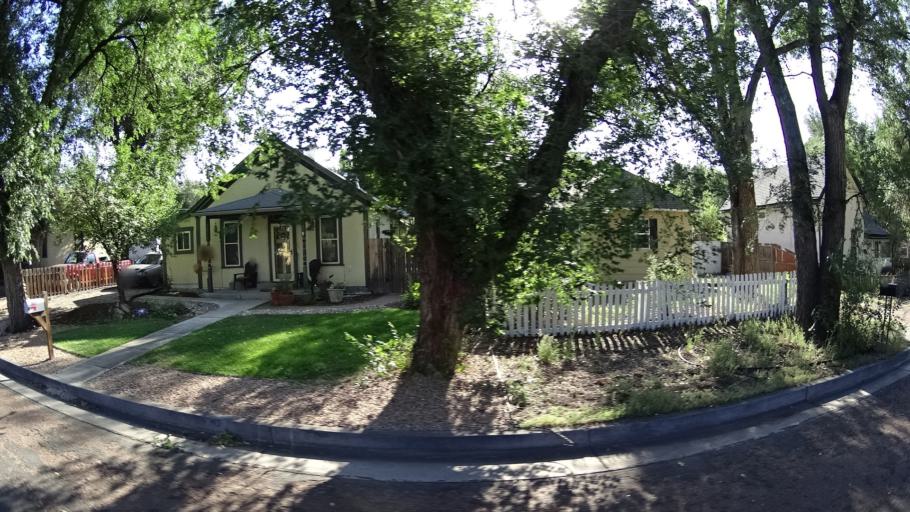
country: US
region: Colorado
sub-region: El Paso County
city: Colorado Springs
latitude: 38.8707
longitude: -104.8296
